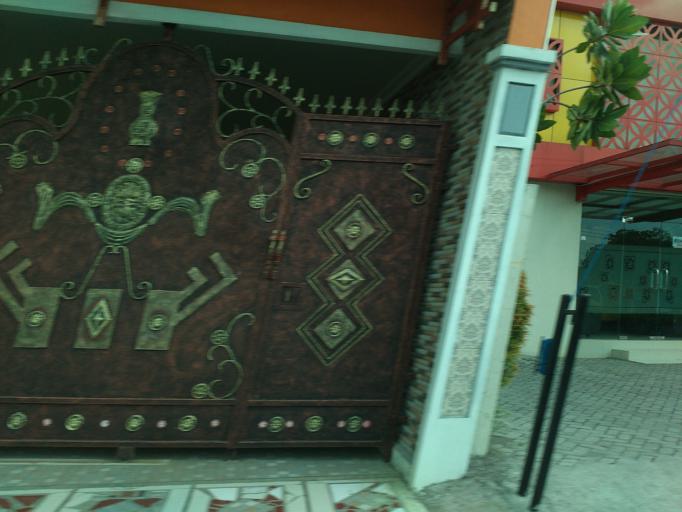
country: ID
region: Central Java
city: Ceper
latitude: -7.6713
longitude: 110.6560
